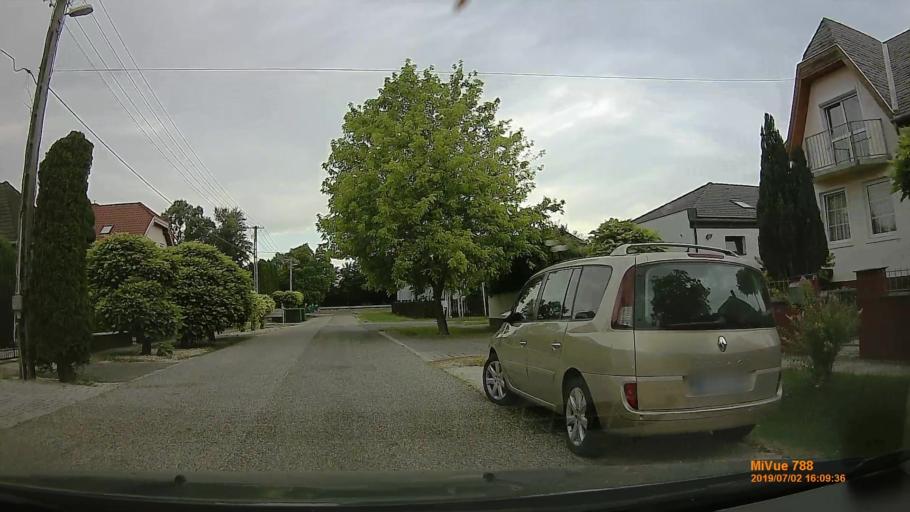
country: HU
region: Gyor-Moson-Sopron
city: Mosonmagyarovar
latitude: 47.8784
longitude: 17.2841
